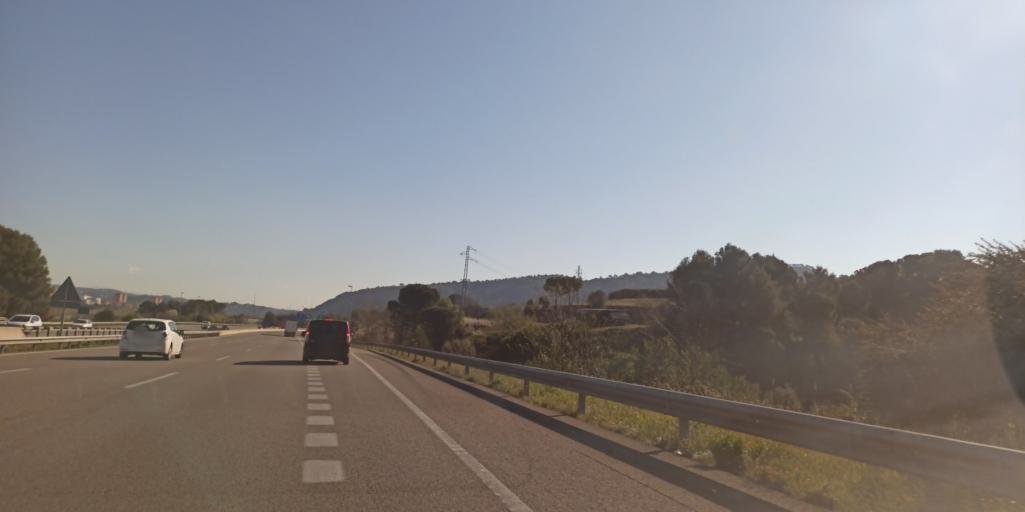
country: ES
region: Catalonia
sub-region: Provincia de Barcelona
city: Castellvi de Rosanes
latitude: 41.4606
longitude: 1.8983
